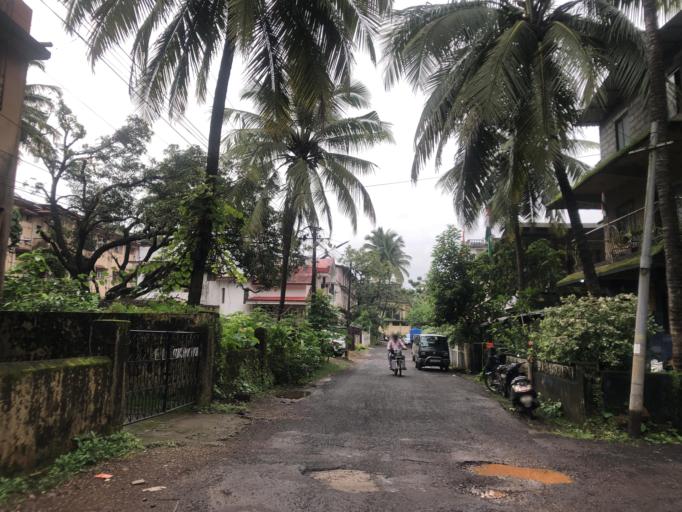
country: IN
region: Goa
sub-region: North Goa
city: Mapuca
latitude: 15.5955
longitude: 73.8039
